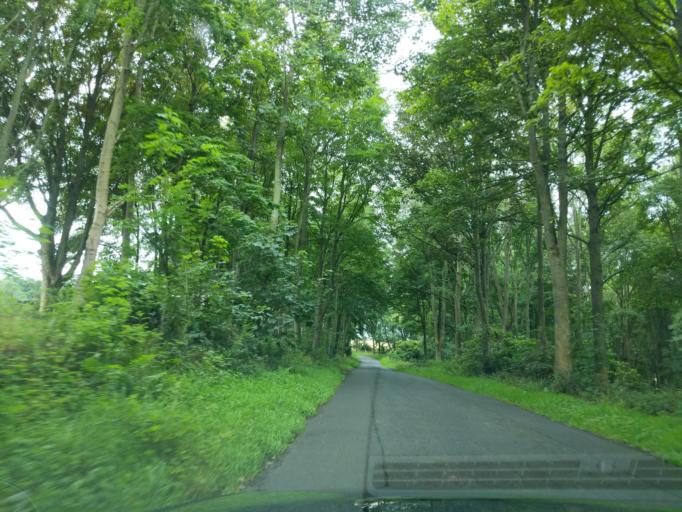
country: GB
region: Scotland
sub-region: Fife
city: Limekilns
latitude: 55.9871
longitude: -3.4888
